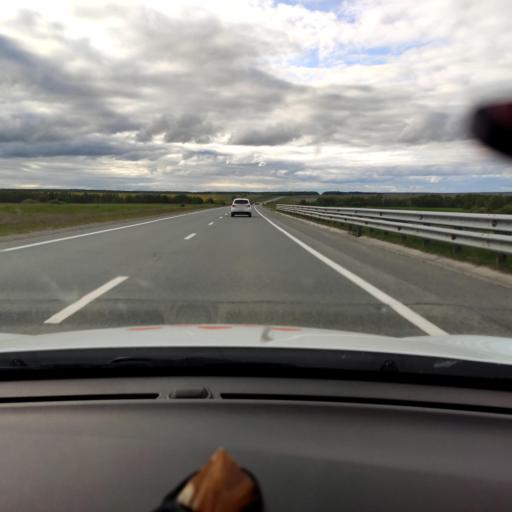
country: RU
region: Tatarstan
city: Pestretsy
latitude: 55.5547
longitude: 49.7378
